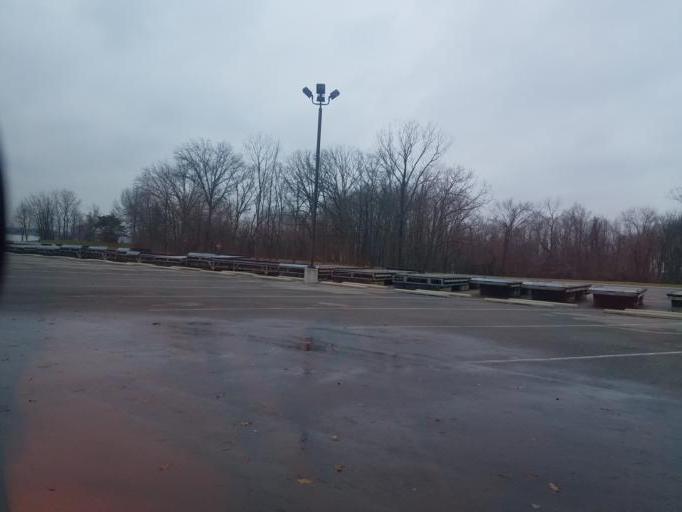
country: US
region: Ohio
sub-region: Delaware County
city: Lewis Center
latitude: 40.1988
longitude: -82.9485
